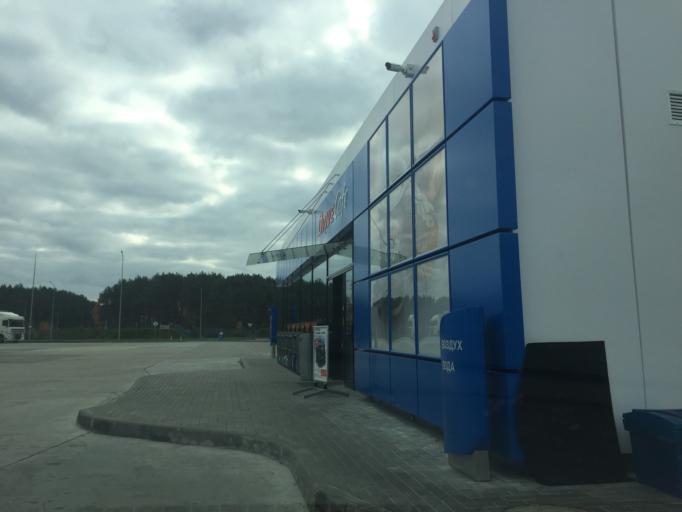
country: BY
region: Grodnenskaya
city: Baruny
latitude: 54.3914
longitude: 26.1215
